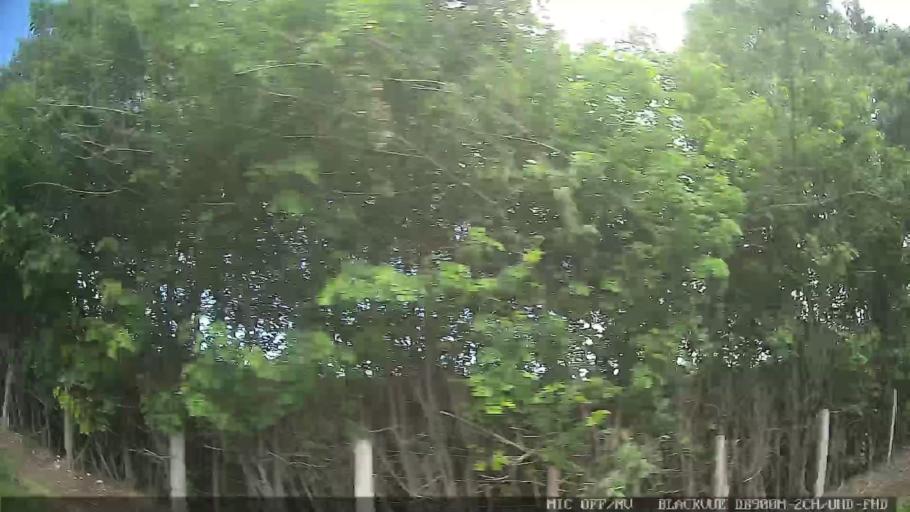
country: BR
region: Sao Paulo
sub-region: Conchas
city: Conchas
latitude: -22.9879
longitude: -47.9933
